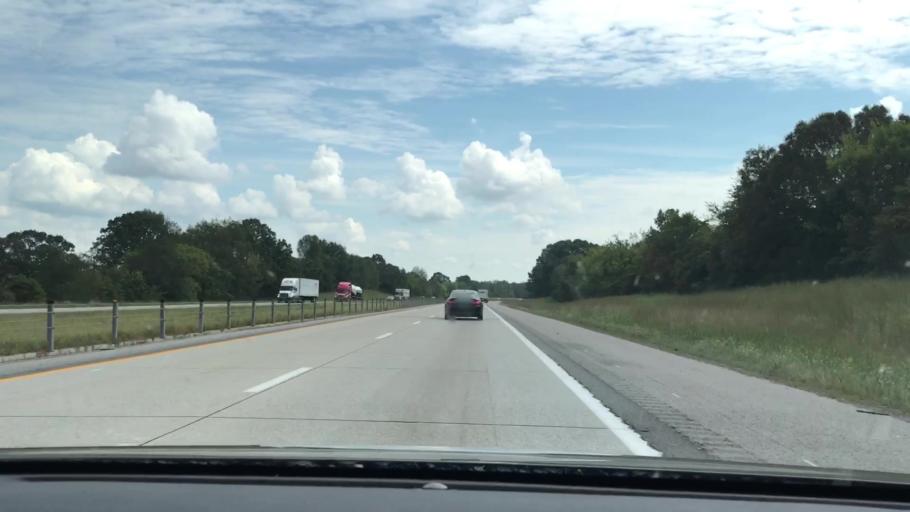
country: US
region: Kentucky
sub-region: Trigg County
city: Cadiz
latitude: 36.8469
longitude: -87.6834
